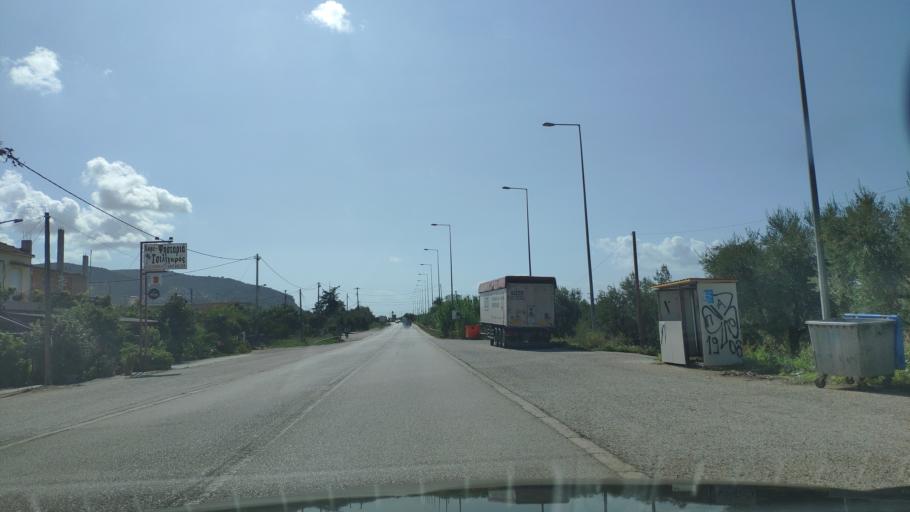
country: GR
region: West Greece
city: Aitoliko
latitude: 38.4769
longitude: 21.3547
